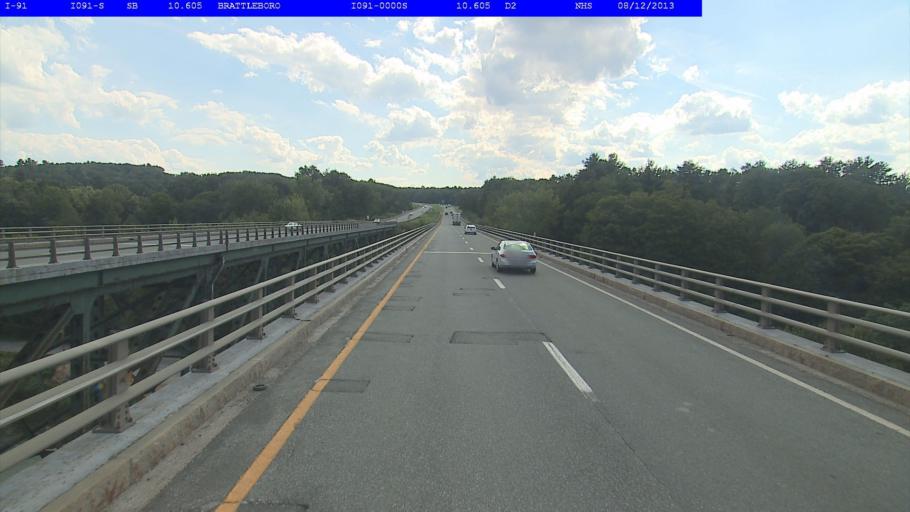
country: US
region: Vermont
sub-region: Windham County
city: Brattleboro
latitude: 42.8748
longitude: -72.5706
